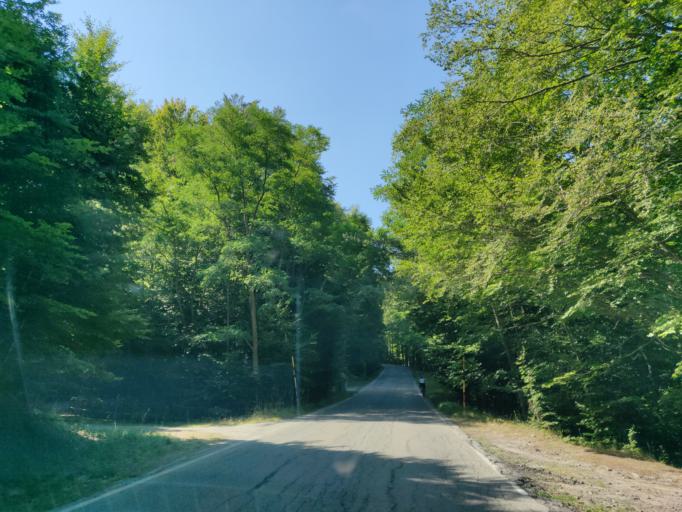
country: IT
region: Tuscany
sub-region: Provincia di Siena
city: Abbadia San Salvatore
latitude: 42.8975
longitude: 11.6139
